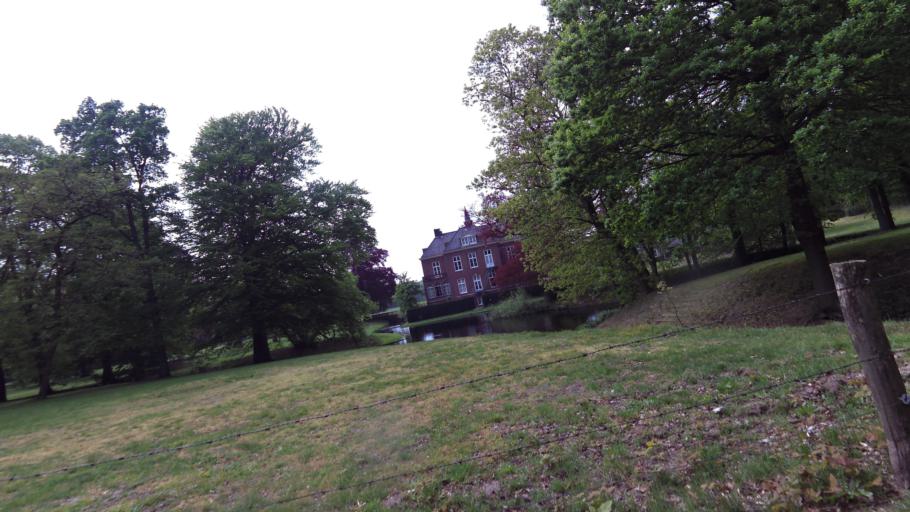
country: NL
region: Gelderland
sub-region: Gemeente Ede
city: Bennekom
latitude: 52.0156
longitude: 5.6782
